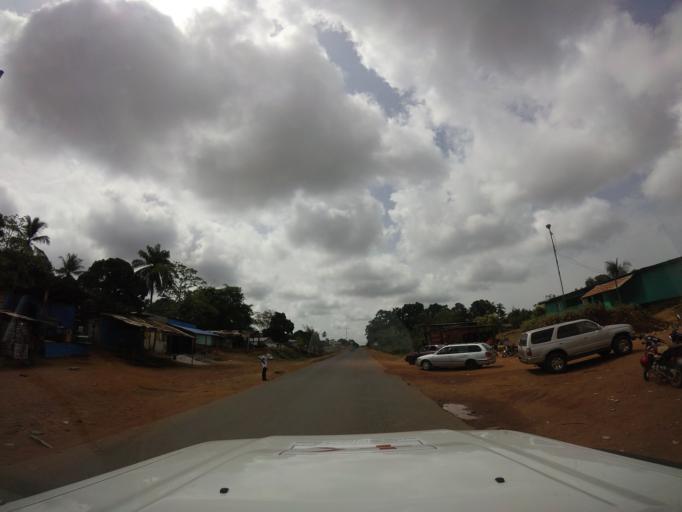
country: LR
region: Montserrado
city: Monrovia
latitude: 6.4489
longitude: -10.8010
